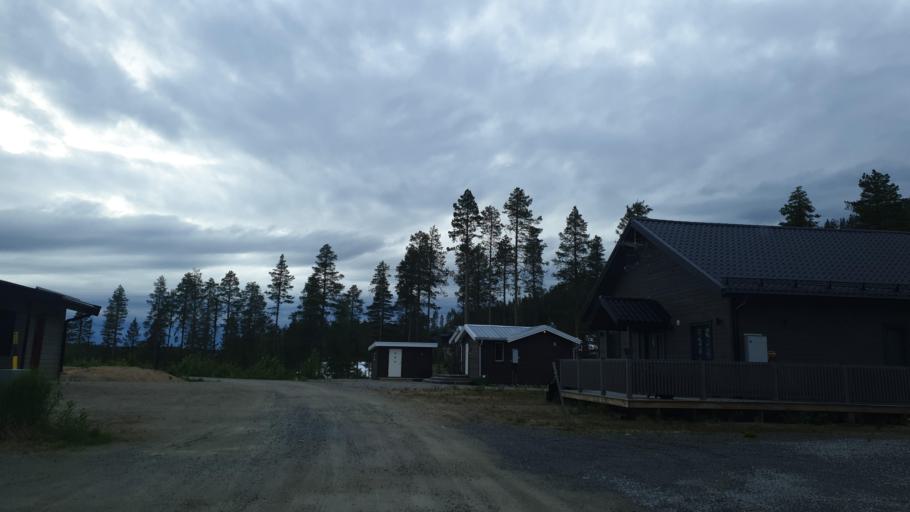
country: SE
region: Norrbotten
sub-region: Jokkmokks Kommun
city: Jokkmokk
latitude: 66.1529
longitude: 19.9958
